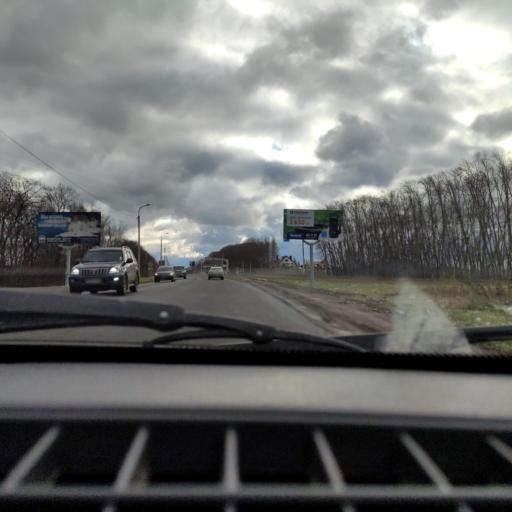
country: RU
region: Bashkortostan
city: Kabakovo
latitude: 54.6338
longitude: 56.0955
